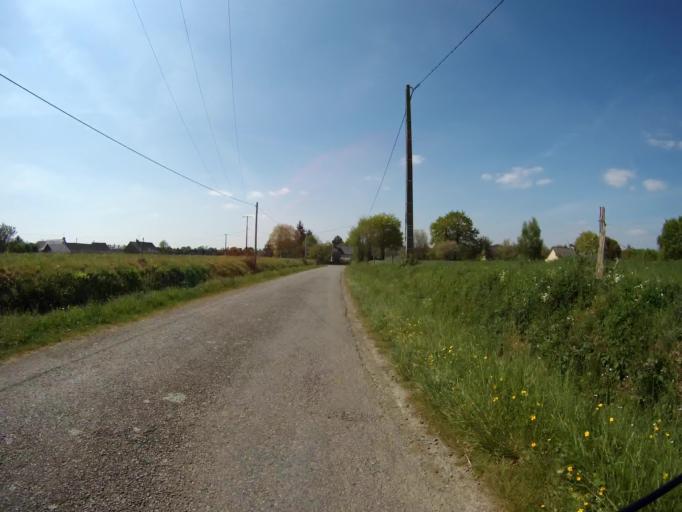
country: FR
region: Brittany
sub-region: Departement d'Ille-et-Vilaine
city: Vern-sur-Seiche
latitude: 48.0325
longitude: -1.6219
